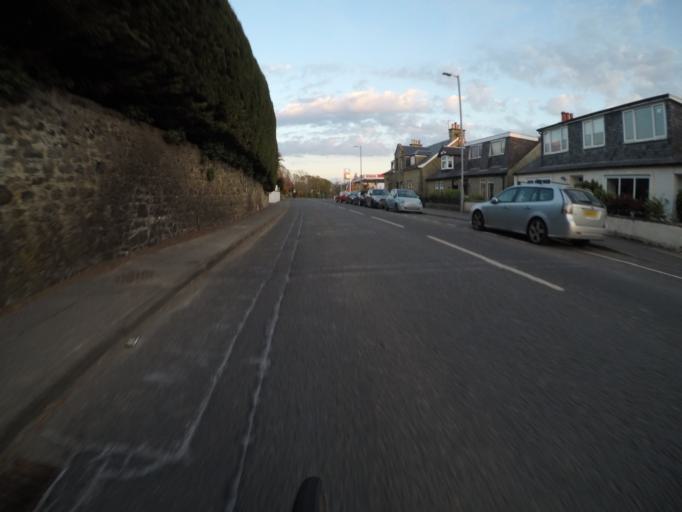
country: GB
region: Scotland
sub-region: South Ayrshire
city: Troon
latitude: 55.5508
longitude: -4.6246
